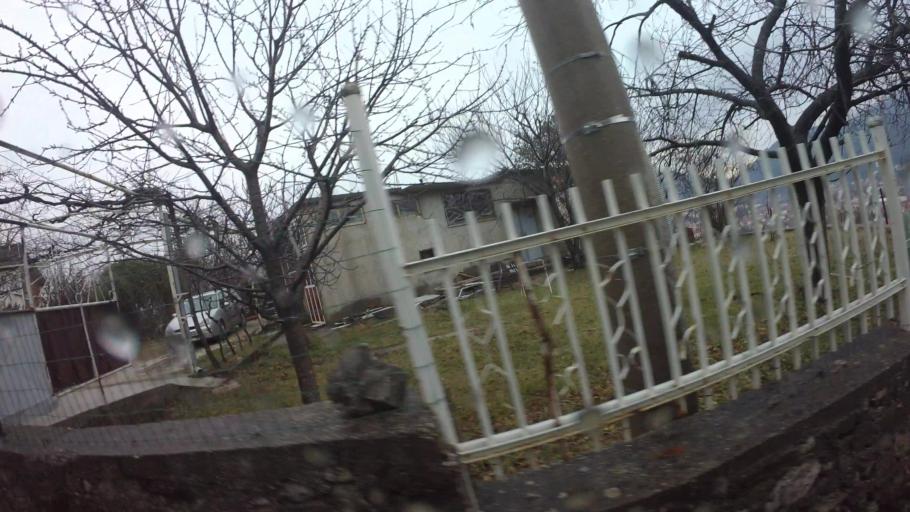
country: BA
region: Federation of Bosnia and Herzegovina
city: Cim
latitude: 43.3559
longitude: 17.7829
